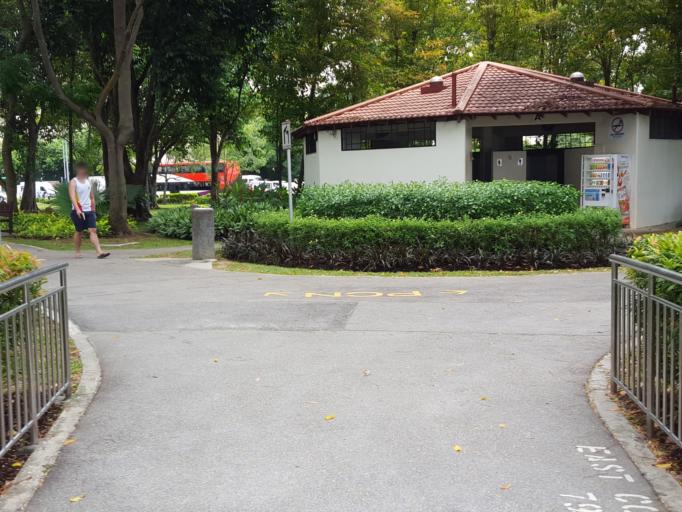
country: SG
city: Singapore
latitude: 1.3388
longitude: 103.9334
